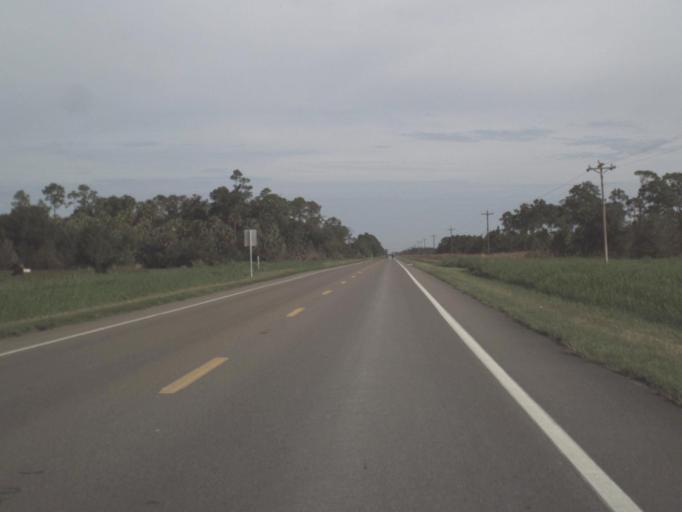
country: US
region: Florida
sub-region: Lee County
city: Fort Myers Shores
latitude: 26.8156
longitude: -81.7602
